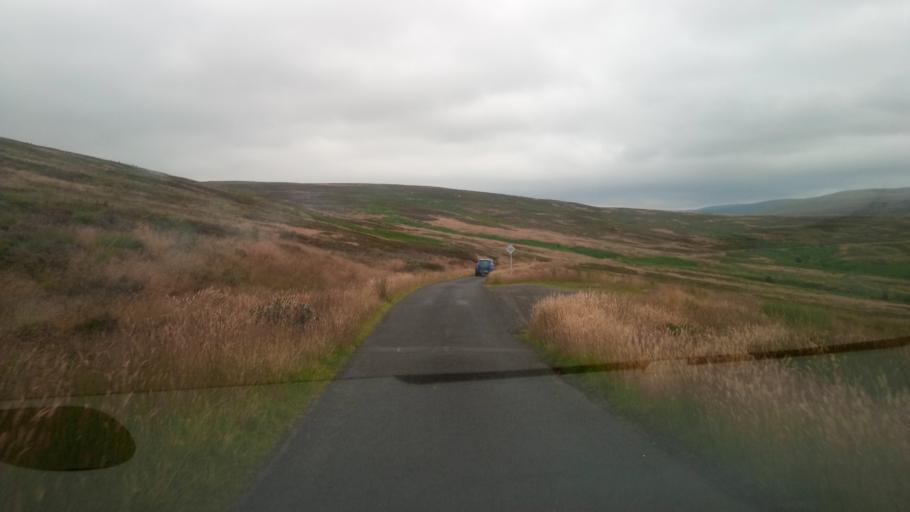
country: GB
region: Scotland
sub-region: Dumfries and Galloway
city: Langholm
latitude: 55.1653
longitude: -2.9614
